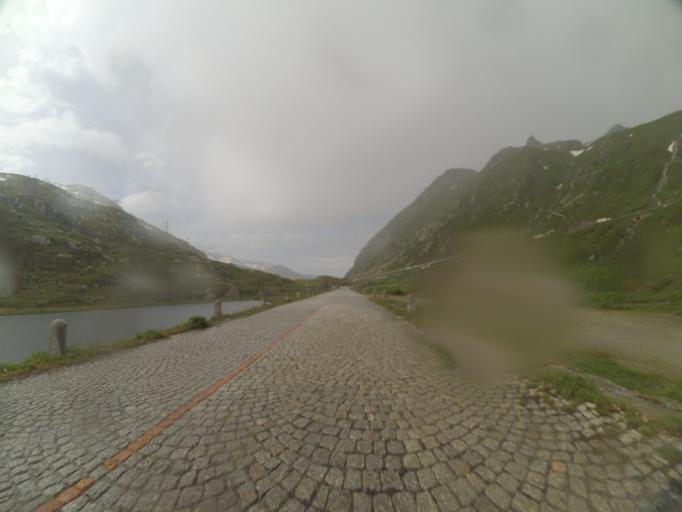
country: CH
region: Ticino
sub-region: Leventina District
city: Airolo
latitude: 46.5710
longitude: 8.5577
